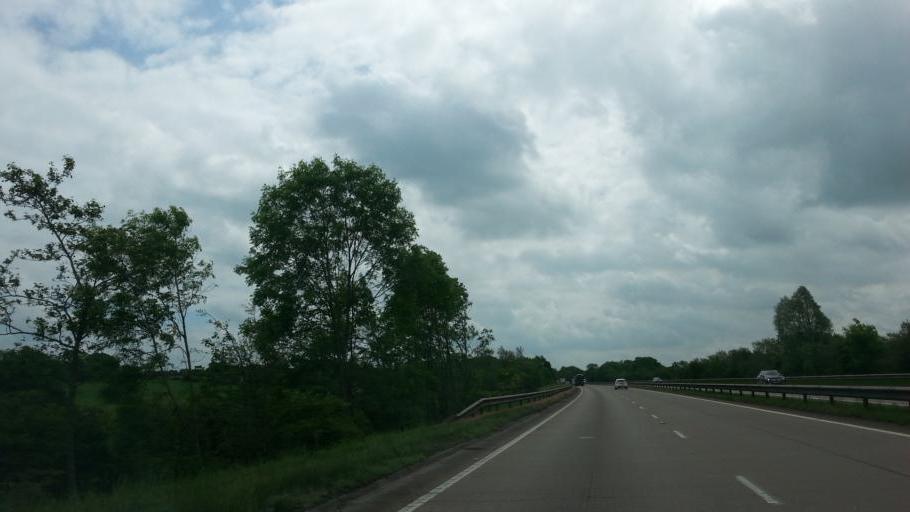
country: GB
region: England
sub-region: Staffordshire
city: Cheadle
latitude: 52.9462
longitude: -2.0092
